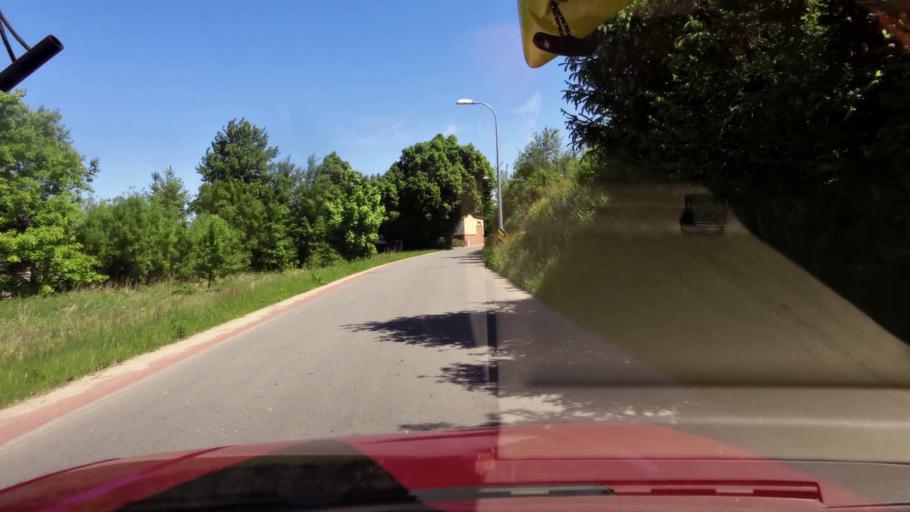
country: PL
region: West Pomeranian Voivodeship
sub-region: Powiat koszalinski
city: Polanow
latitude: 54.0438
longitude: 16.7248
